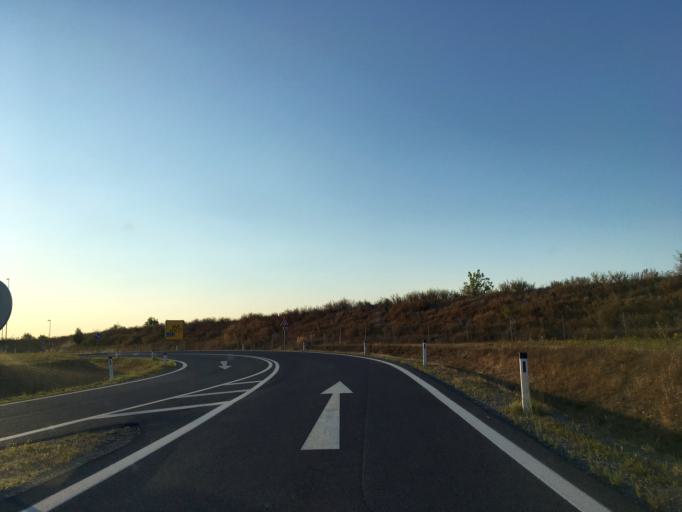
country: AT
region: Burgenland
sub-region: Politischer Bezirk Neusiedl am See
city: Potzneusiedl
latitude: 48.0329
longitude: 16.9653
